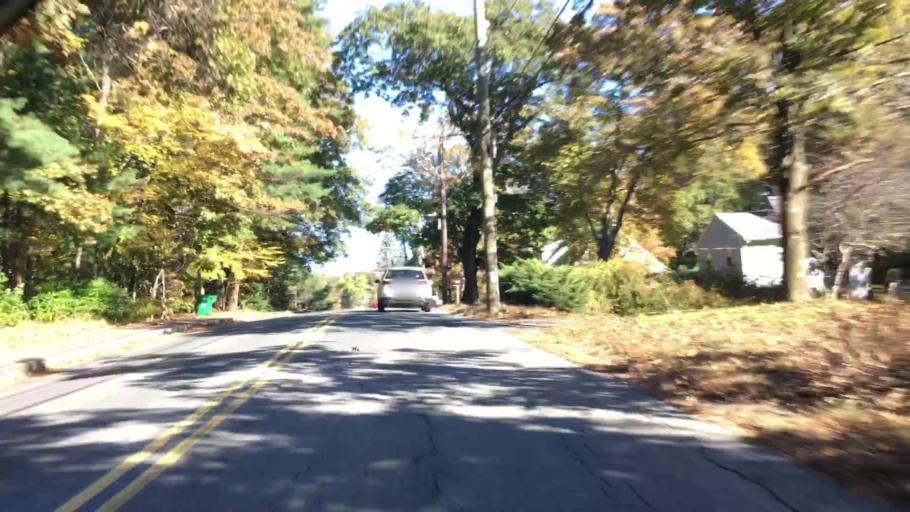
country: US
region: Massachusetts
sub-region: Middlesex County
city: Ashland
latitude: 42.2685
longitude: -71.4631
